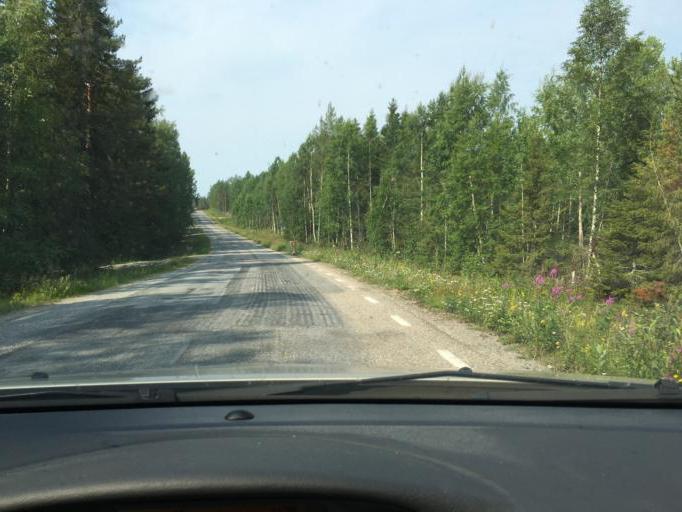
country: SE
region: Norrbotten
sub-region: Kalix Kommun
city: Rolfs
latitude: 65.7789
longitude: 22.9425
